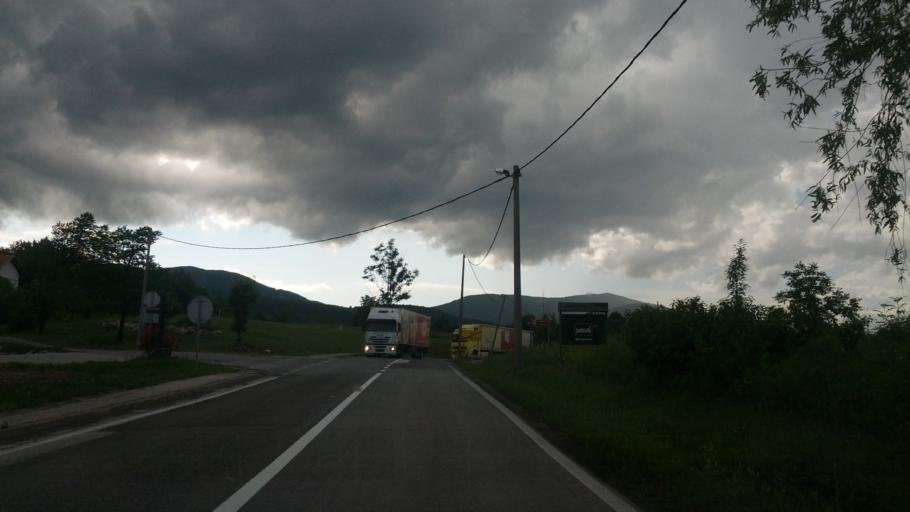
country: HR
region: Licko-Senjska
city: Jezerce
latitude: 44.9563
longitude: 15.6665
